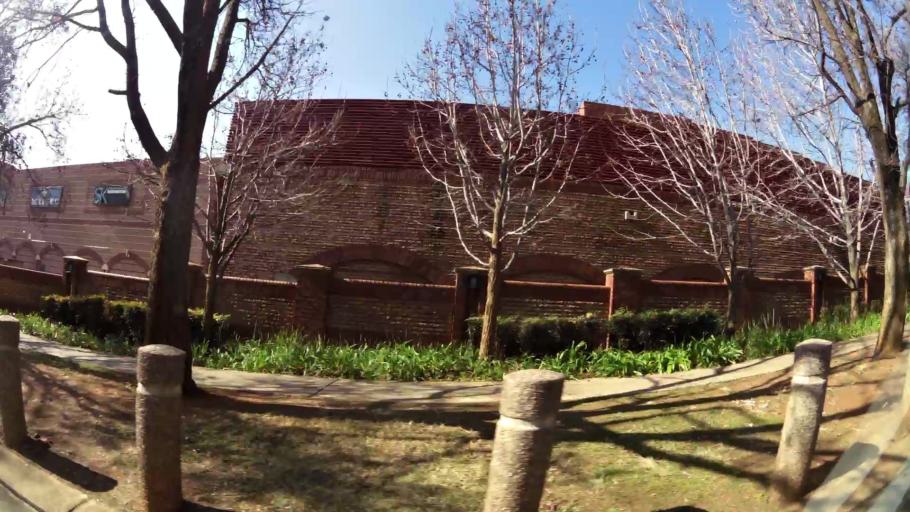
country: ZA
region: Gauteng
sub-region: City of Tshwane Metropolitan Municipality
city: Pretoria
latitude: -25.7734
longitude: 28.2336
